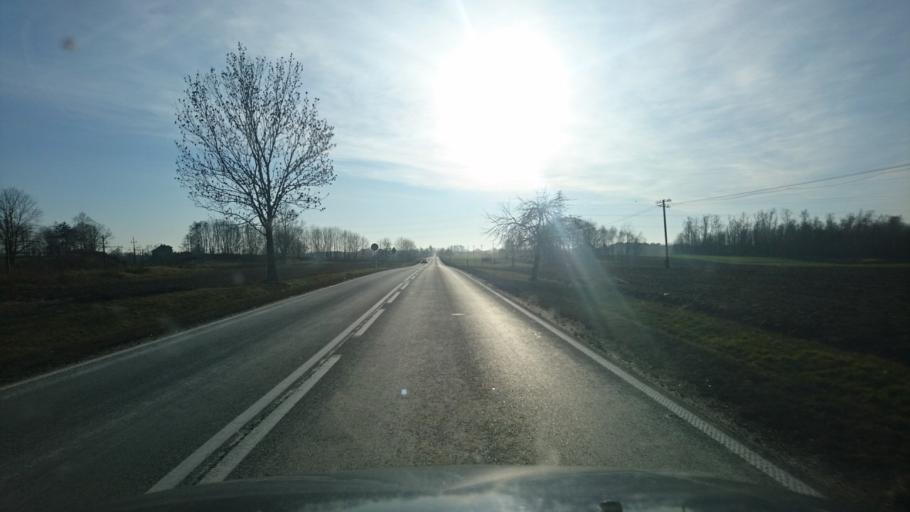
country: PL
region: Opole Voivodeship
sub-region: Powiat oleski
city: Dalachow
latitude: 51.0621
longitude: 18.6001
